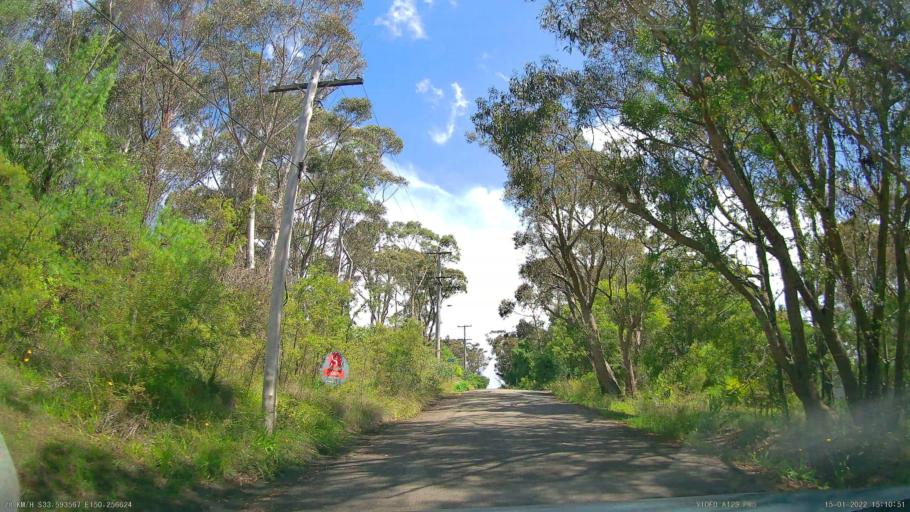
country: AU
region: New South Wales
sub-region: Blue Mountains Municipality
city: Blackheath
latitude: -33.5937
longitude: 150.2566
